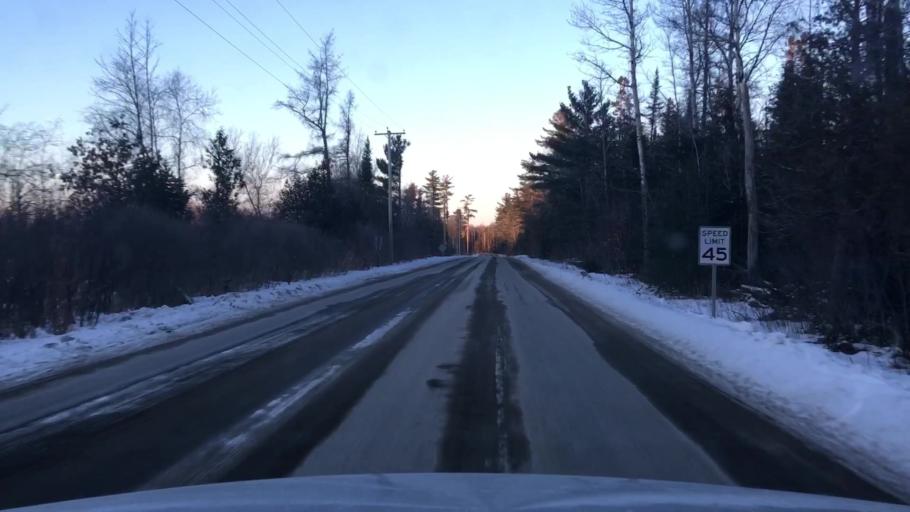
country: US
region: Maine
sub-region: Penobscot County
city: Orrington
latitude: 44.7088
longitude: -68.7544
